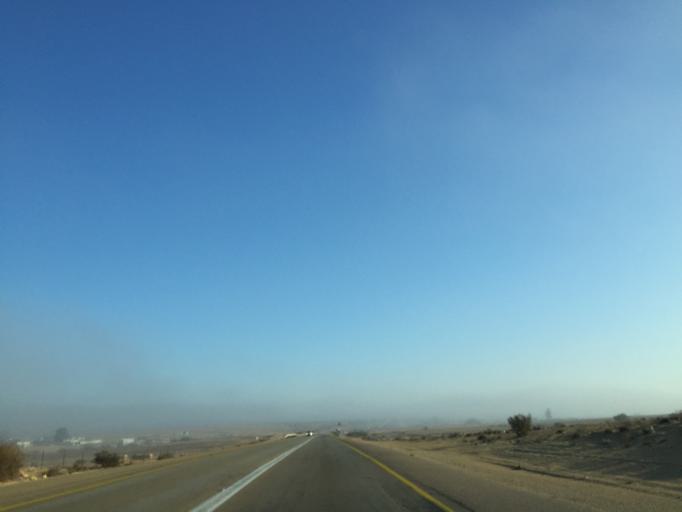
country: IL
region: Southern District
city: Yeroham
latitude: 31.0047
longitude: 34.9487
